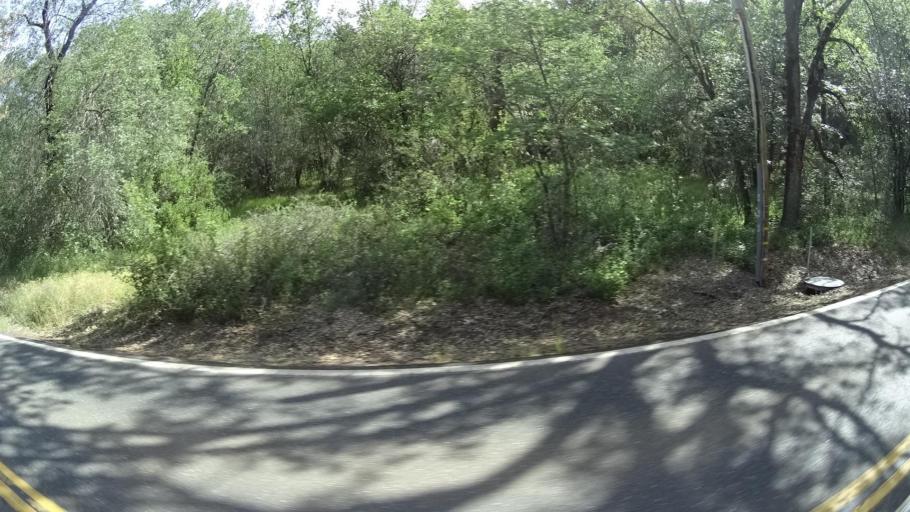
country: US
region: California
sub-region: Lake County
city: Cobb
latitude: 38.8973
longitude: -122.7405
